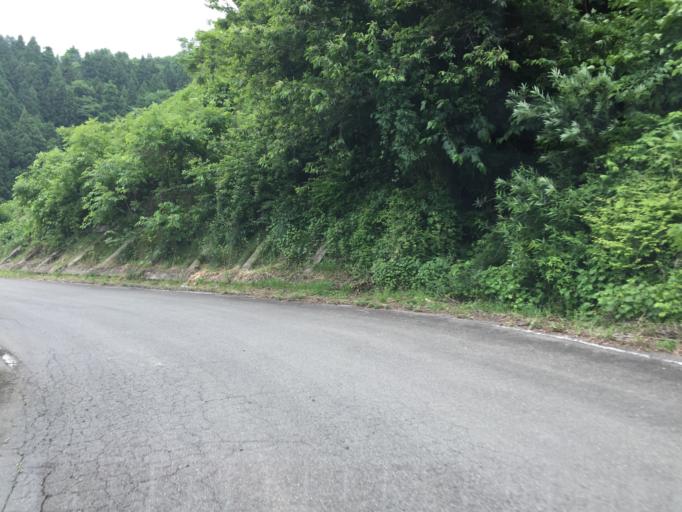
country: JP
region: Miyagi
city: Marumori
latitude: 37.7986
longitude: 140.7730
